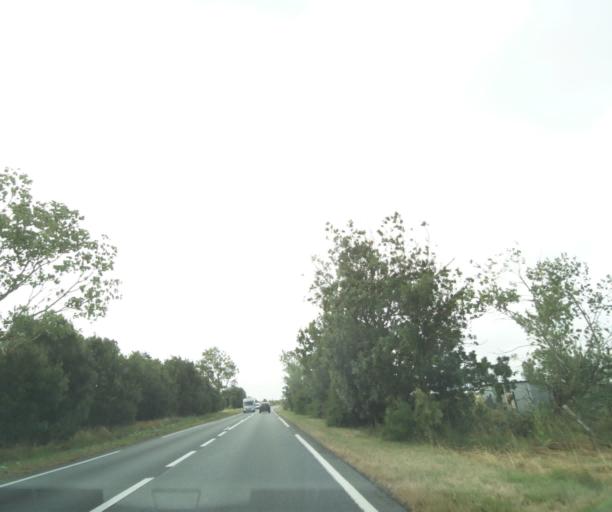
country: FR
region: Poitou-Charentes
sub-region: Departement de la Charente-Maritime
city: Andilly
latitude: 46.2564
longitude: -1.0665
